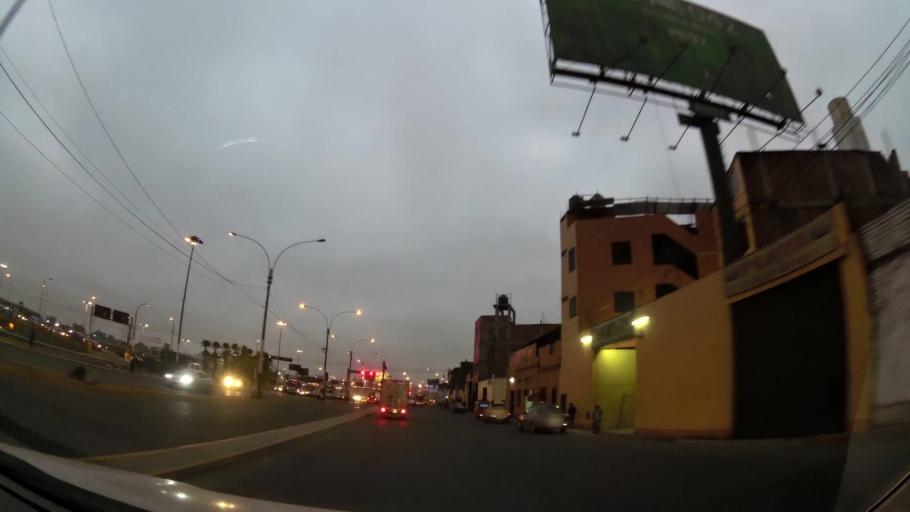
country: PE
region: Lima
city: Lima
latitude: -12.0411
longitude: -77.0199
